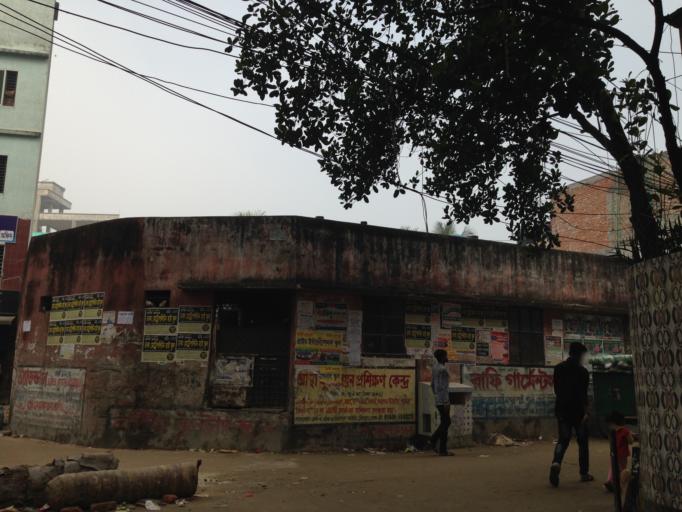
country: BD
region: Dhaka
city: Azimpur
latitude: 23.8024
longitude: 90.3462
